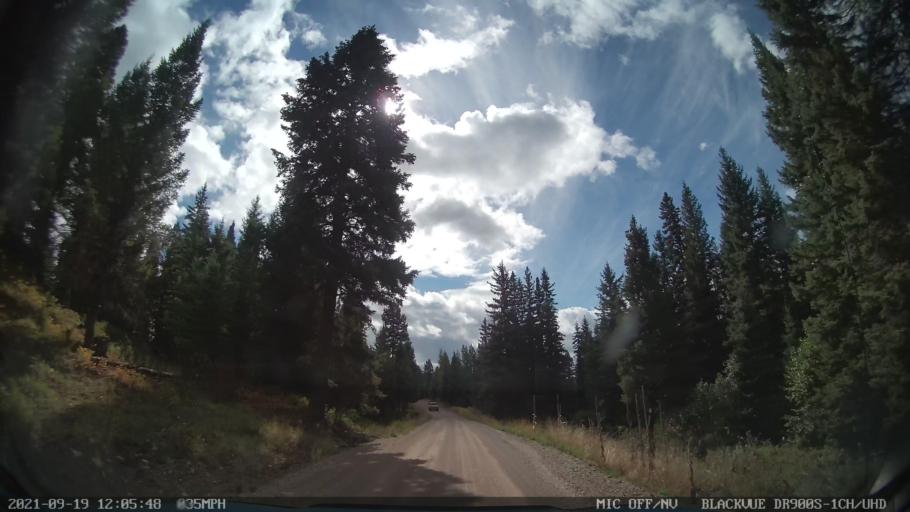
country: US
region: Montana
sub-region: Missoula County
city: Seeley Lake
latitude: 47.1890
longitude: -113.4235
